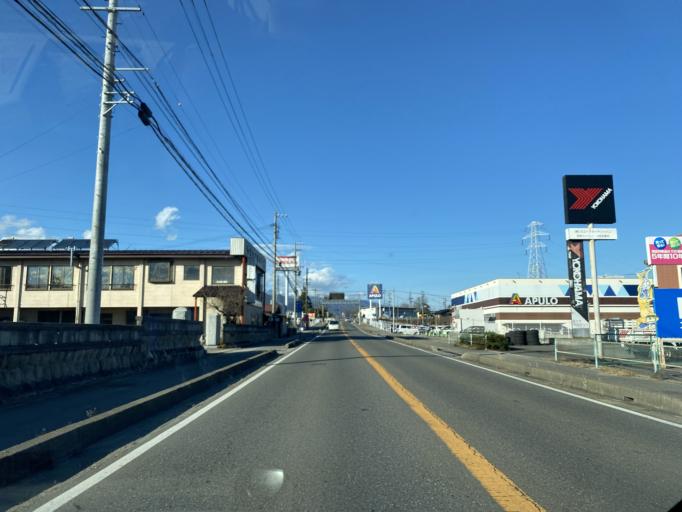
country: JP
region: Nagano
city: Omachi
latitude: 36.4846
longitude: 137.8516
